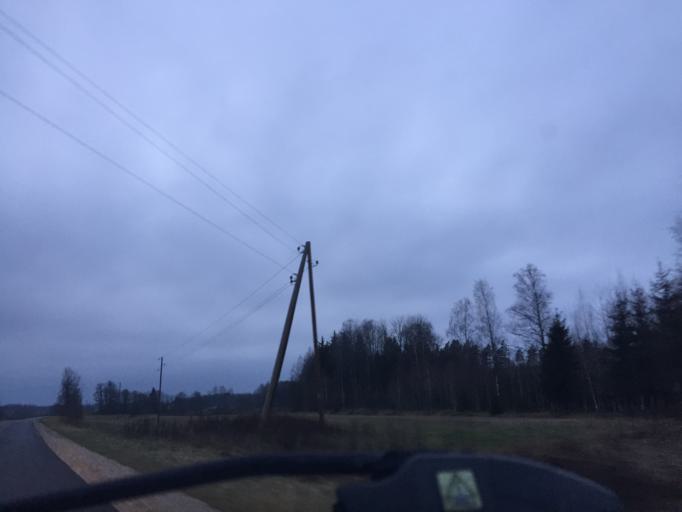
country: LV
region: Aloja
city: Aloja
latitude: 57.6309
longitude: 24.8670
